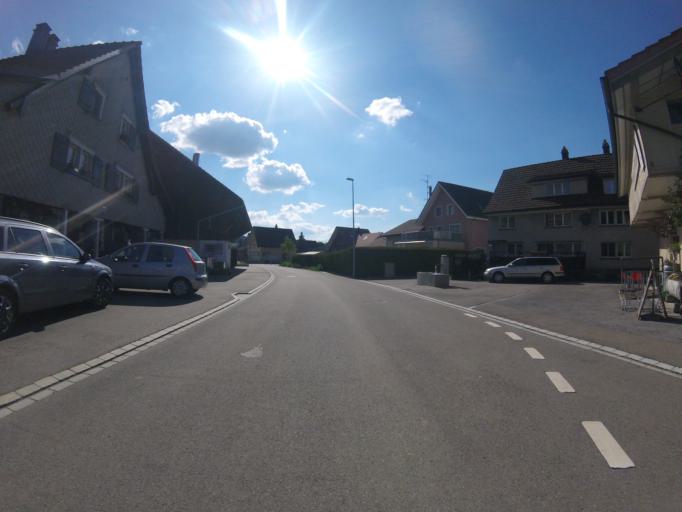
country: CH
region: Saint Gallen
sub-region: Wahlkreis Wil
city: Degersheim
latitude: 47.3951
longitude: 9.2034
